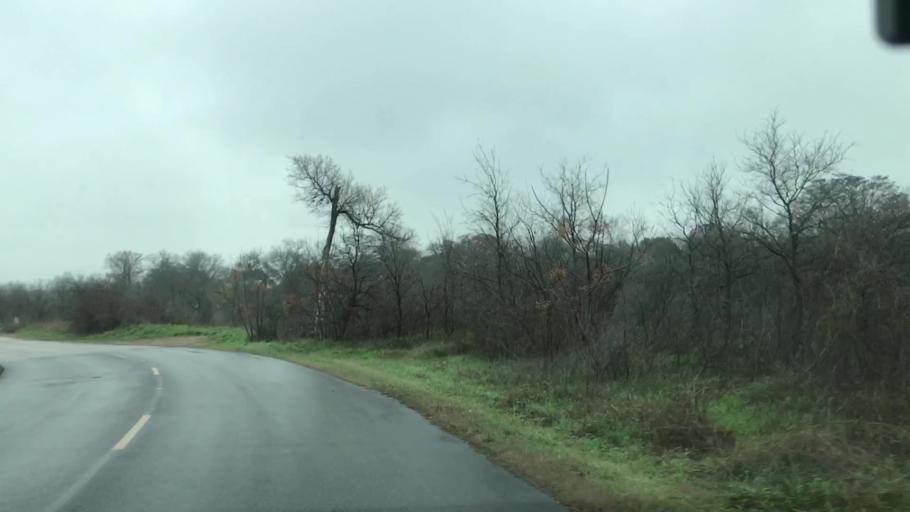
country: US
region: Texas
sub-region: Hays County
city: San Marcos
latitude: 29.8926
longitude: -97.9004
